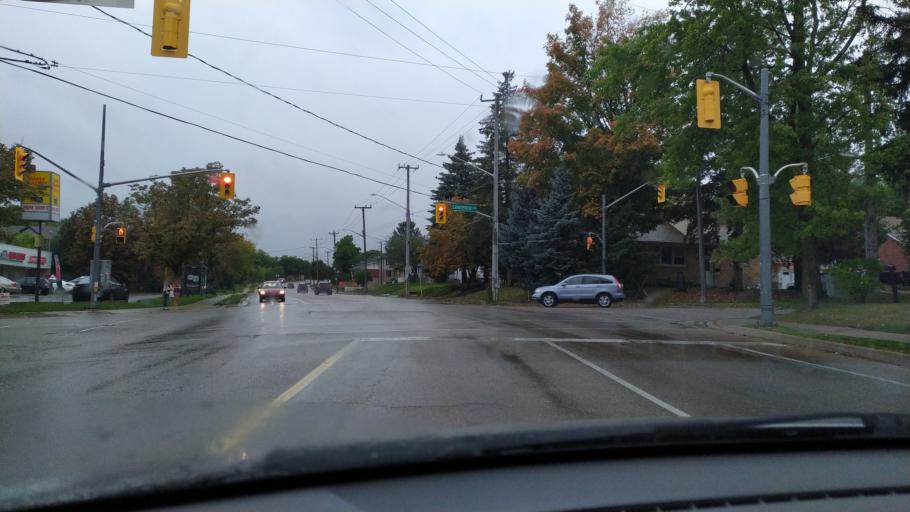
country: CA
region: Ontario
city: Kitchener
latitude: 43.4423
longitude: -80.5142
